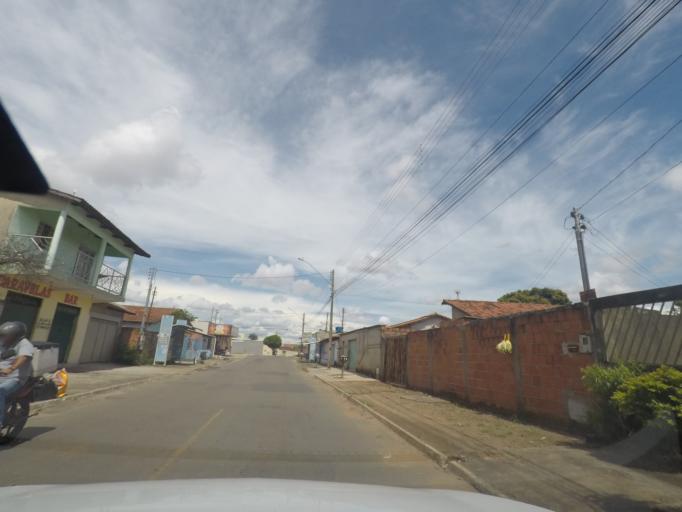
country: BR
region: Goias
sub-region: Goiania
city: Goiania
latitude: -16.7554
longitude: -49.3490
